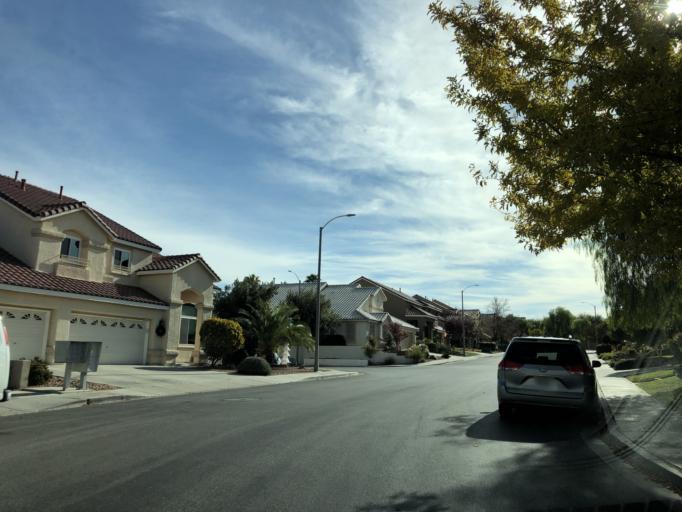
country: US
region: Nevada
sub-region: Clark County
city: Whitney
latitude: 36.0146
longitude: -115.0801
